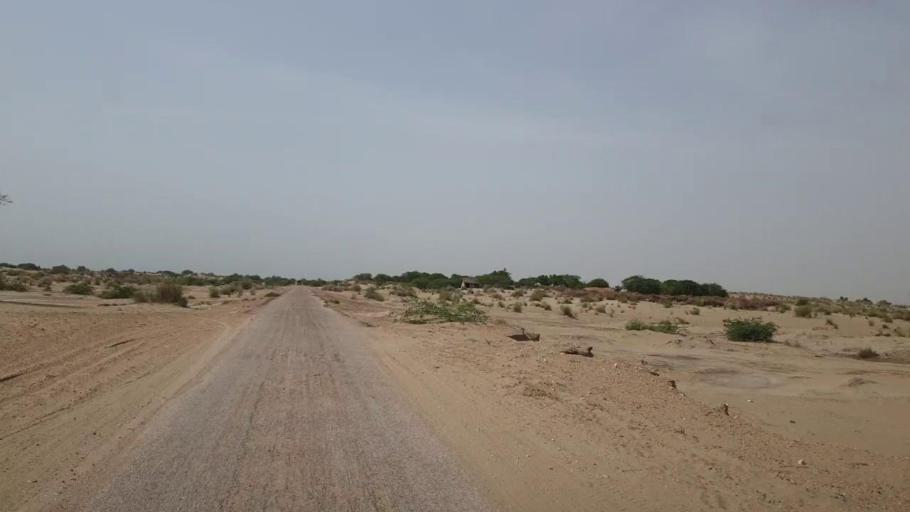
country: PK
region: Sindh
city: Bandhi
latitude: 26.5434
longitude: 68.3858
